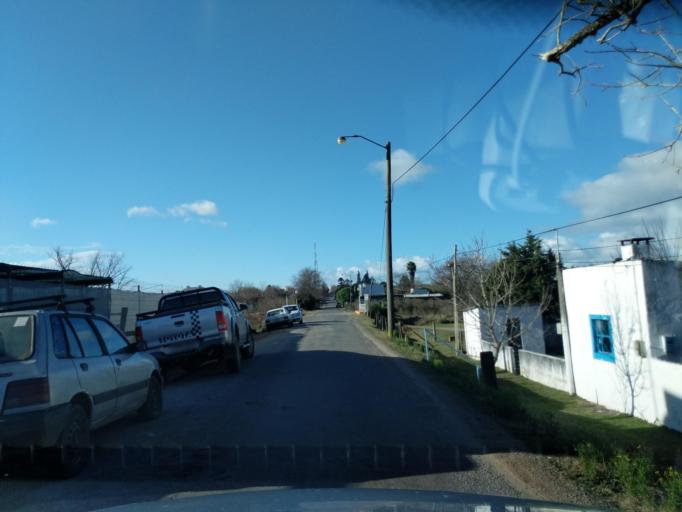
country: UY
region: Florida
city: Florida
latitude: -34.1071
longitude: -56.2224
